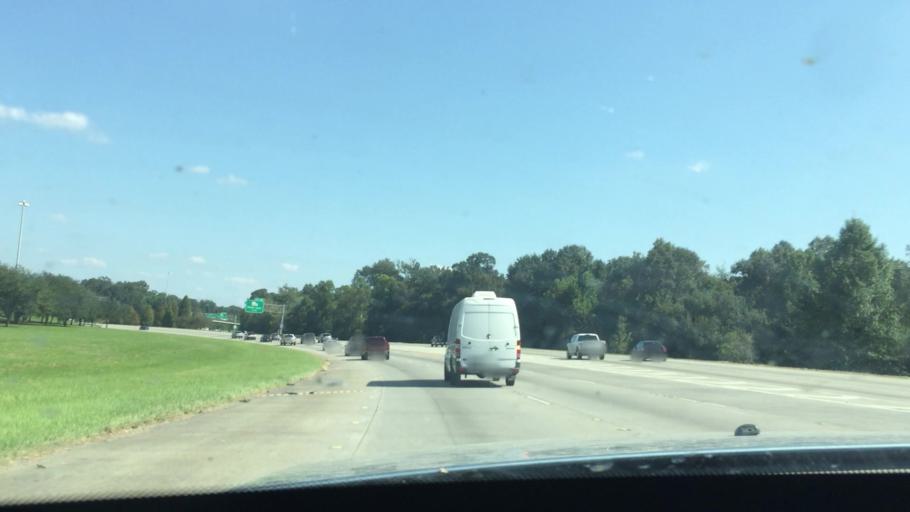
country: US
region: Louisiana
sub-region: East Baton Rouge Parish
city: Westminster
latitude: 30.4191
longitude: -91.1204
